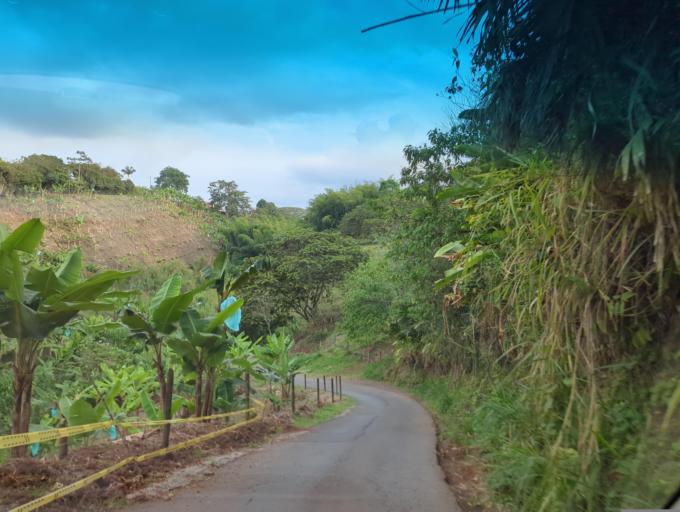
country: CO
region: Risaralda
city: Pereira
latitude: 4.8261
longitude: -75.7593
